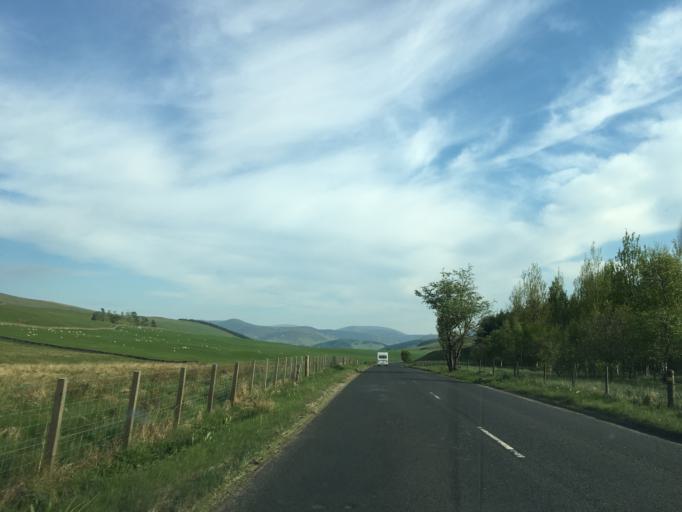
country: GB
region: Scotland
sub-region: South Lanarkshire
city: Biggar
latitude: 55.6429
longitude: -3.4269
